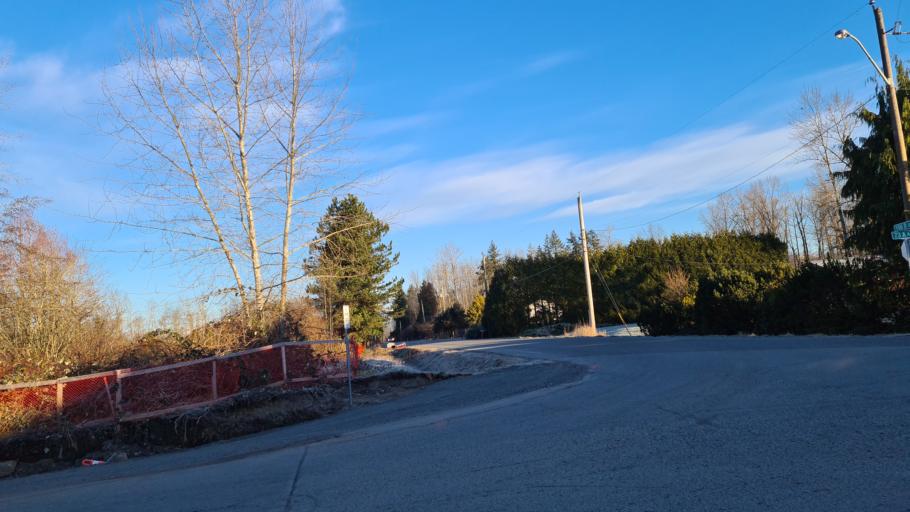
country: CA
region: British Columbia
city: Langley
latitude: 49.1355
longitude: -122.6724
